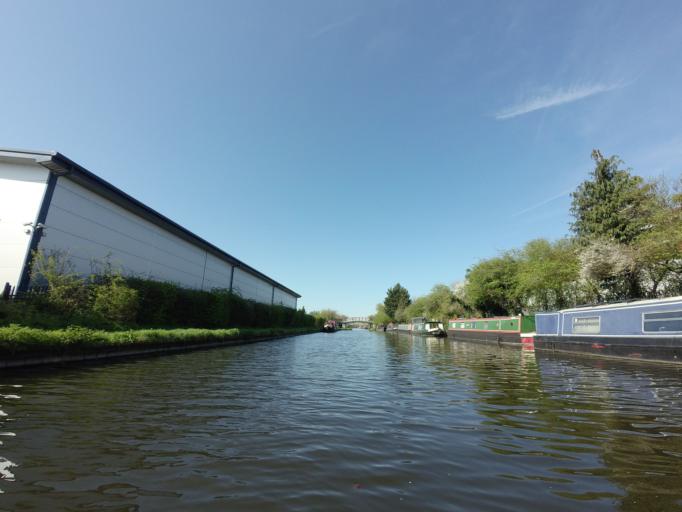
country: GB
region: England
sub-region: Greater London
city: Uxbridge
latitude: 51.5373
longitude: -0.4878
